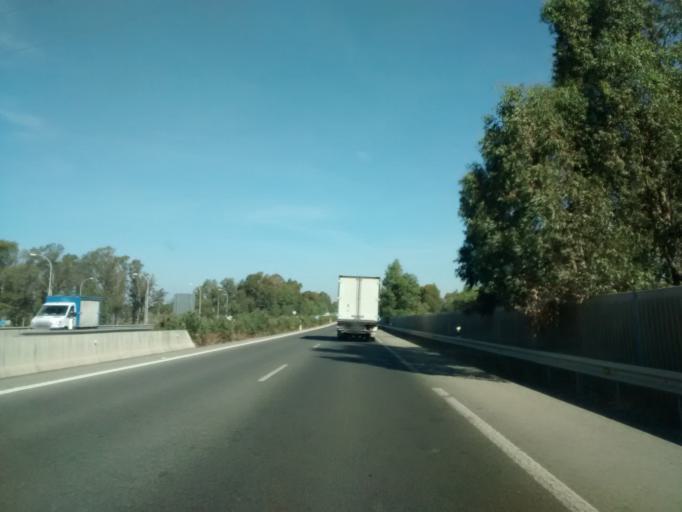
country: ES
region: Andalusia
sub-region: Provincia de Cadiz
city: Chiclana de la Frontera
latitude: 36.3905
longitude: -6.1196
